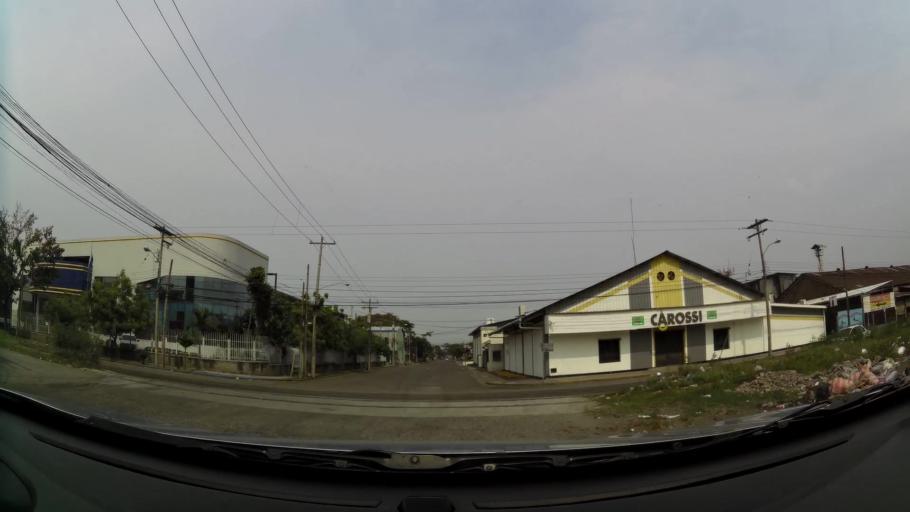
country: HN
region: Cortes
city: San Pedro Sula
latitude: 15.4928
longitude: -88.0252
